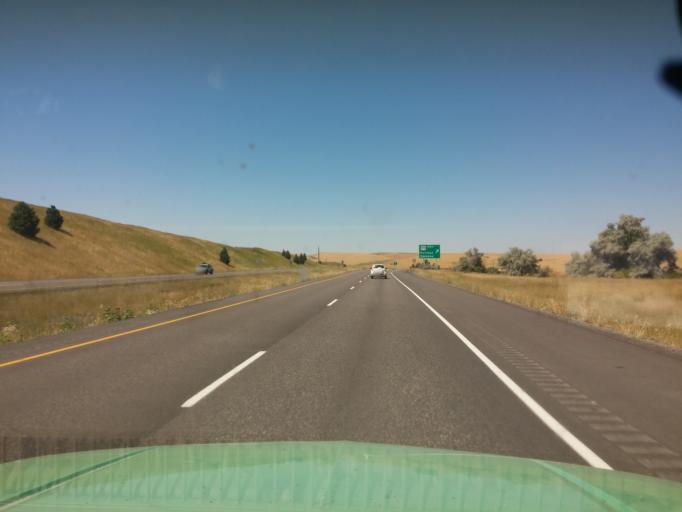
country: US
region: Idaho
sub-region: Nez Perce County
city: Lewiston
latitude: 46.4683
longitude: -117.0283
